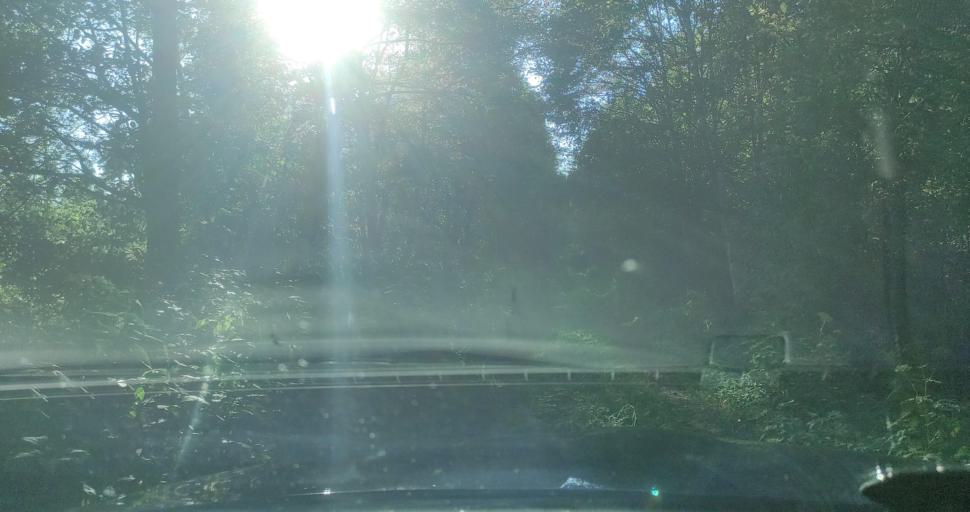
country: LV
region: Skrunda
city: Skrunda
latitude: 56.6794
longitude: 21.9779
